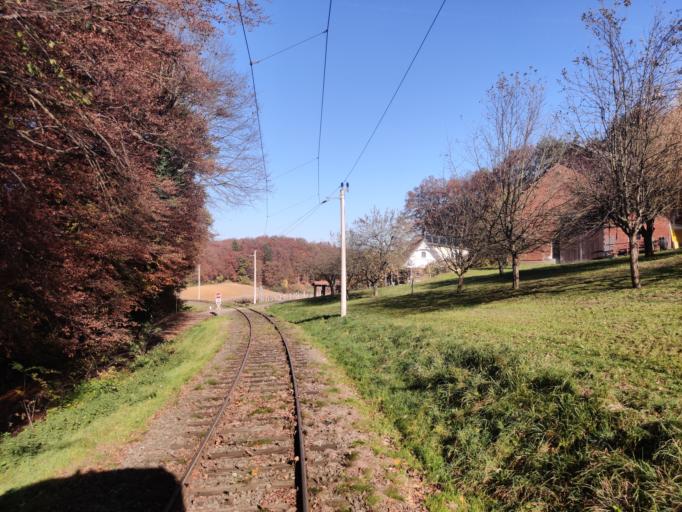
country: AT
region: Styria
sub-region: Politischer Bezirk Suedoststeiermark
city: Maierdorf
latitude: 46.9079
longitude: 15.8390
